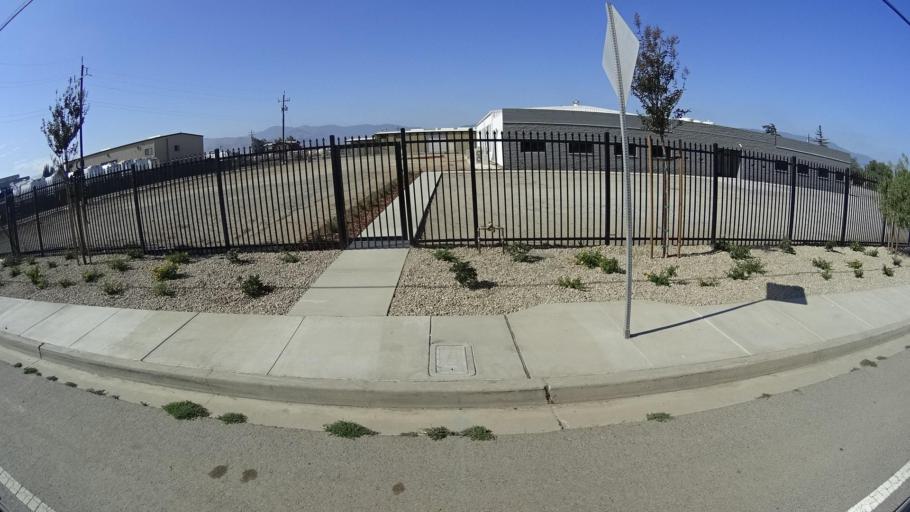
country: US
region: California
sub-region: Monterey County
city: Greenfield
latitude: 36.3320
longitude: -121.2531
